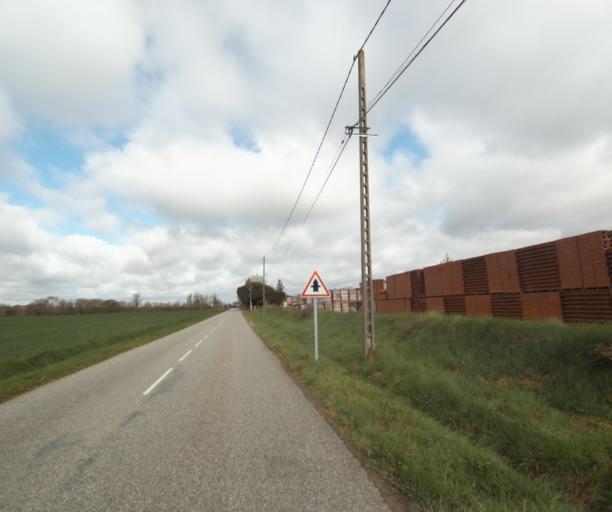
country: FR
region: Midi-Pyrenees
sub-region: Departement de l'Ariege
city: Saverdun
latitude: 43.2444
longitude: 1.5630
